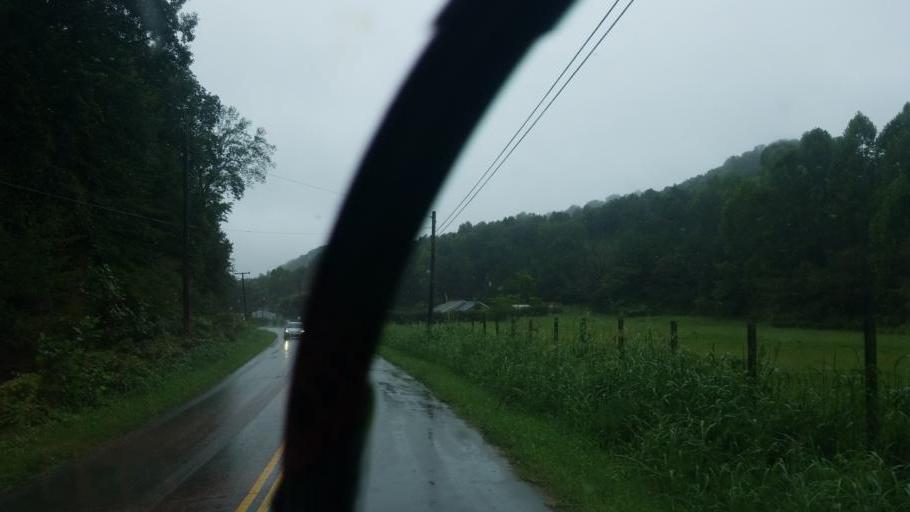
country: US
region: Ohio
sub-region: Scioto County
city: West Portsmouth
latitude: 38.7426
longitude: -83.0761
